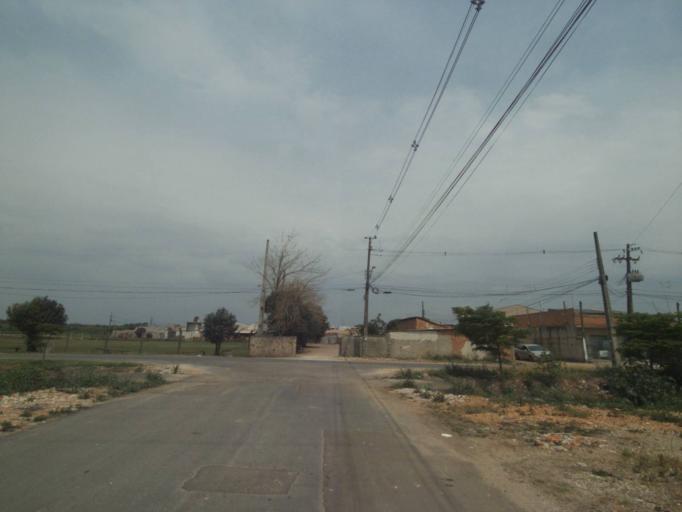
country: BR
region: Parana
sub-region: Pinhais
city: Pinhais
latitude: -25.4867
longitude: -49.1962
